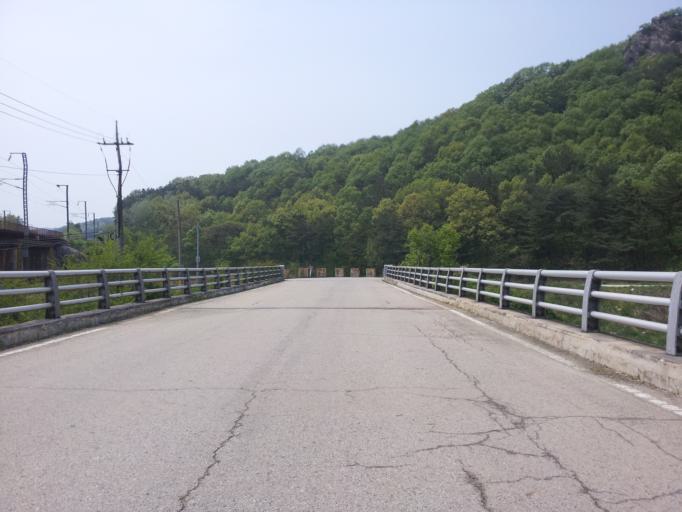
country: KR
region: Daejeon
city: Daejeon
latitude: 36.2648
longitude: 127.2972
